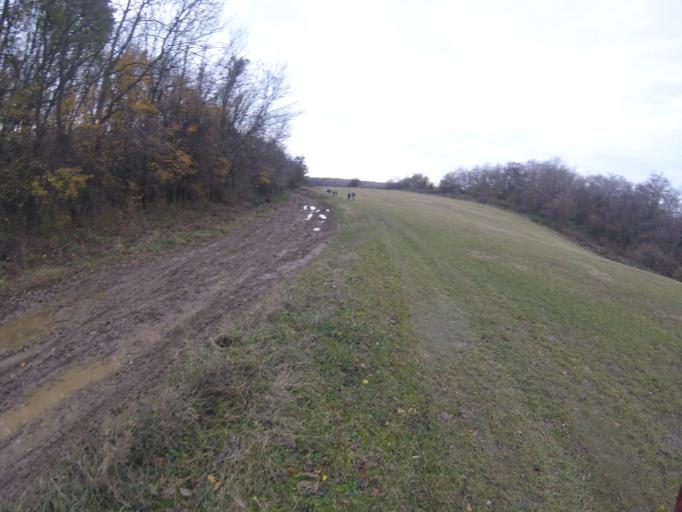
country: HU
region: Tolna
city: Szentgalpuszta
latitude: 46.3284
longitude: 18.6471
